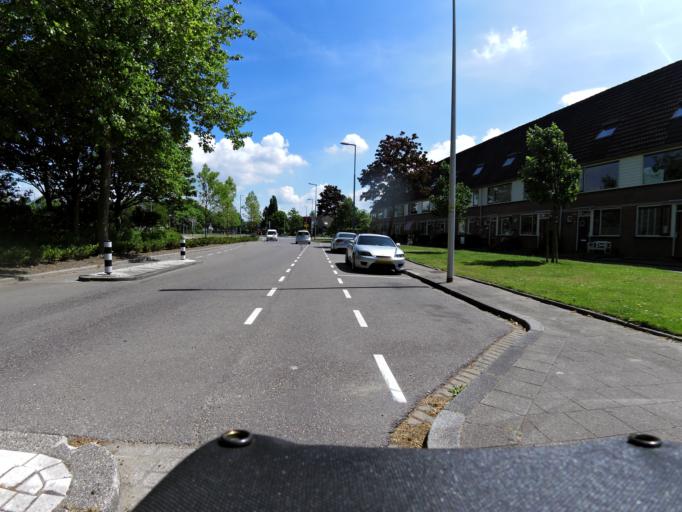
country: NL
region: South Holland
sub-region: Gemeente Maassluis
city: Maassluis
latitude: 51.9053
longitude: 4.2356
